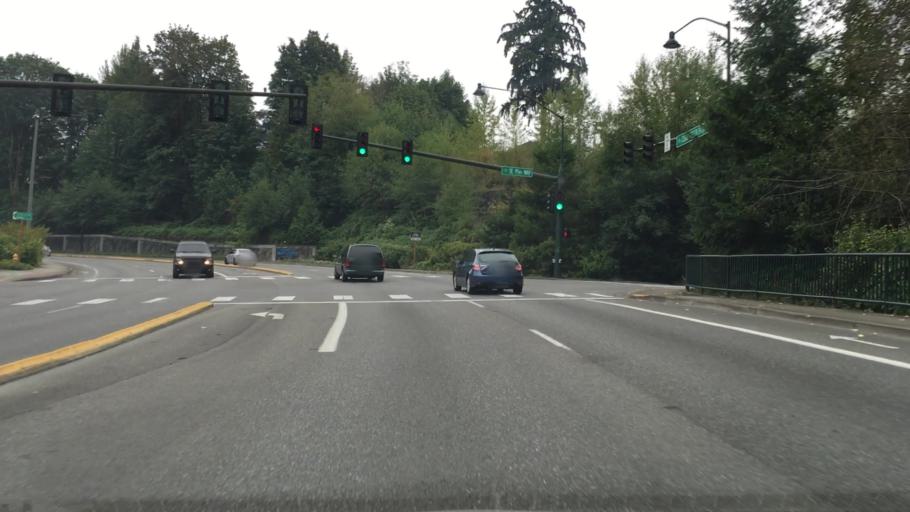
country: US
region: Washington
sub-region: King County
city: Newcastle
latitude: 47.5164
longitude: -122.1593
